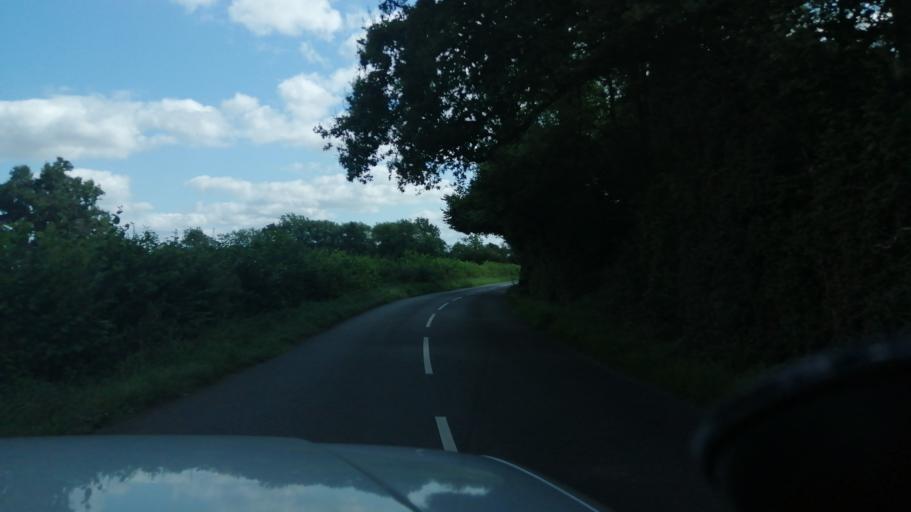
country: GB
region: England
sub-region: Herefordshire
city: Moccas
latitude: 52.0756
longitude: -2.9361
